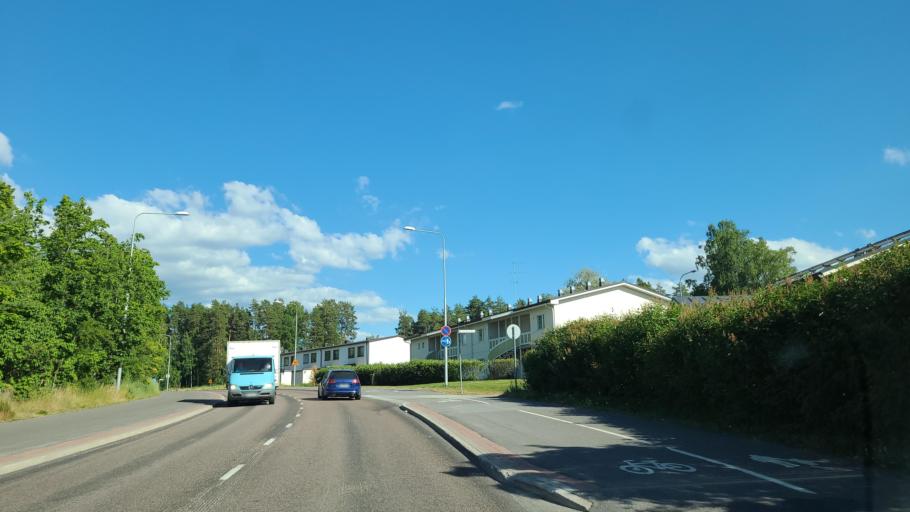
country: FI
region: Central Finland
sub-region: Jyvaeskylae
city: Jyvaeskylae
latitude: 62.2434
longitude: 25.7899
